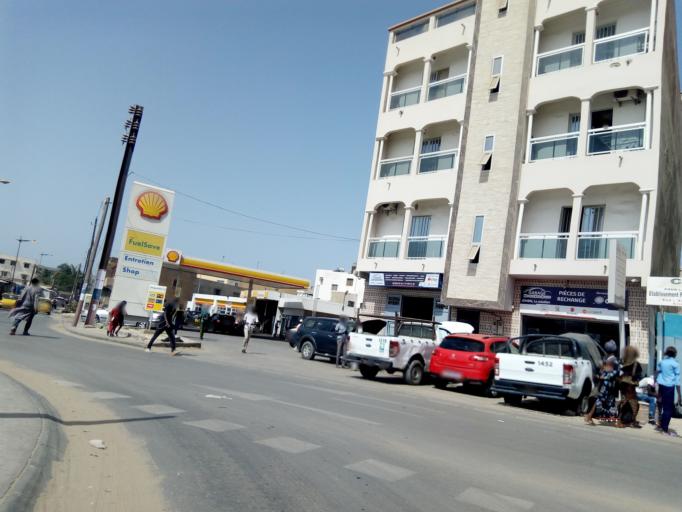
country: SN
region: Dakar
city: Grand Dakar
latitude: 14.7044
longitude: -17.4518
